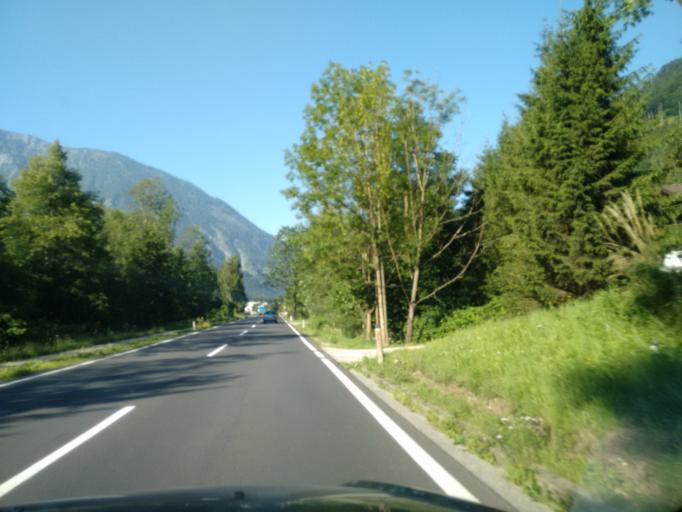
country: AT
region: Upper Austria
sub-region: Politischer Bezirk Gmunden
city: Ebensee
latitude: 47.7606
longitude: 13.7068
